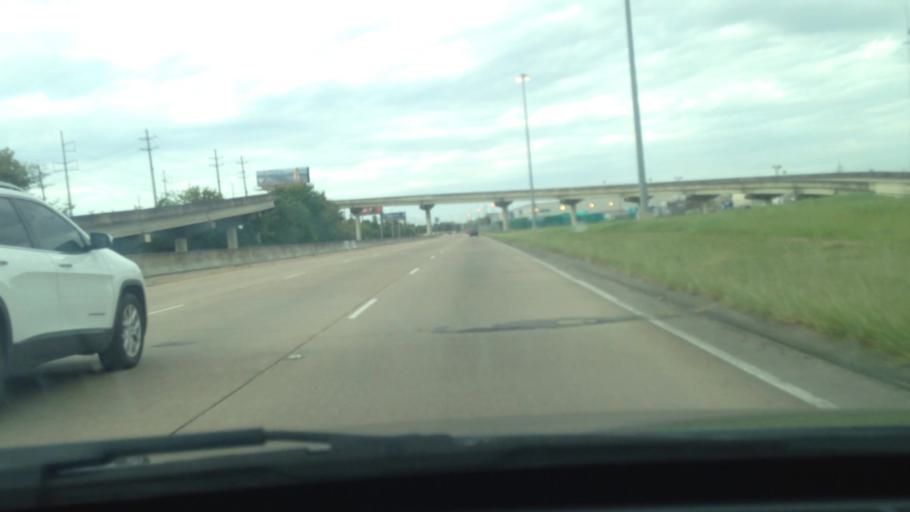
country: US
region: Louisiana
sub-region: Jefferson Parish
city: Jefferson
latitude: 29.9699
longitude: -90.1428
